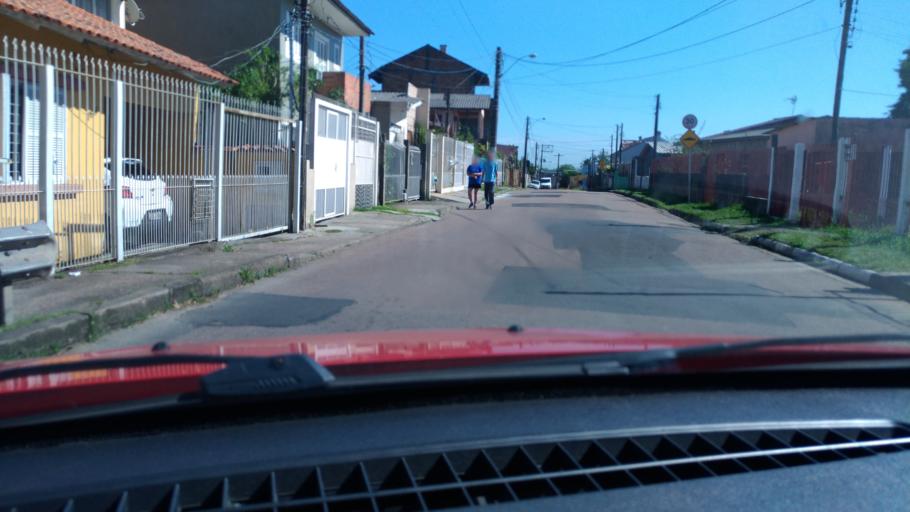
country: BR
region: Rio Grande do Sul
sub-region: Cachoeirinha
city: Cachoeirinha
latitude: -30.0365
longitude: -51.1274
